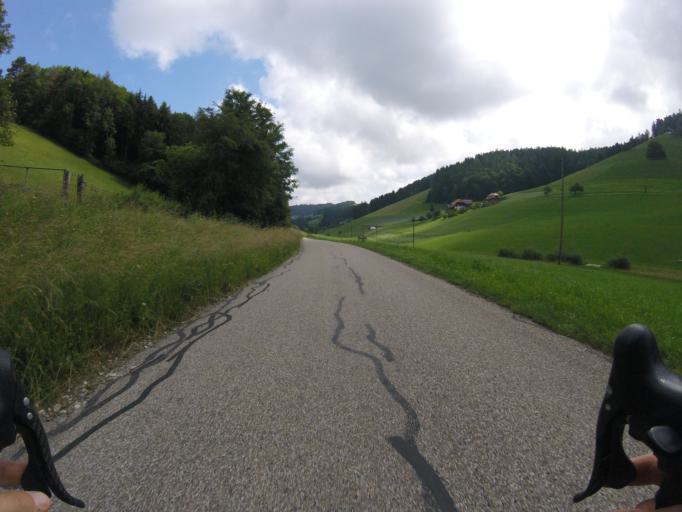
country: CH
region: Bern
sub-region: Emmental District
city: Krauchthal
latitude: 46.9944
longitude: 7.5857
